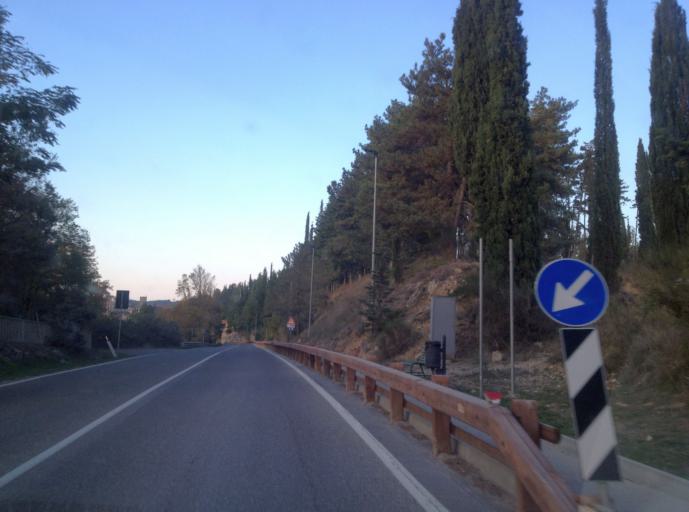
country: IT
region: Tuscany
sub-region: Provincia di Siena
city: Castellina in Chianti
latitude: 43.4568
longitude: 11.2924
